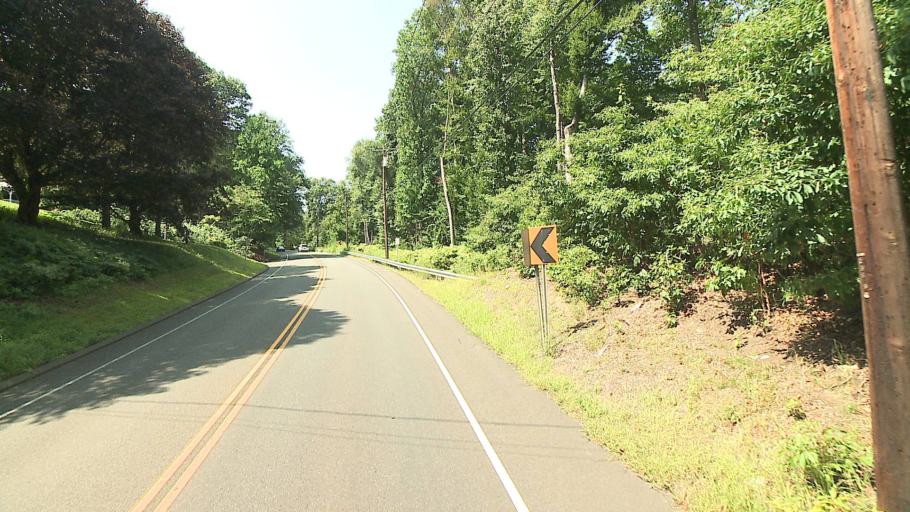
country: US
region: Connecticut
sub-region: Fairfield County
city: Shelton
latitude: 41.3374
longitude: -73.1256
